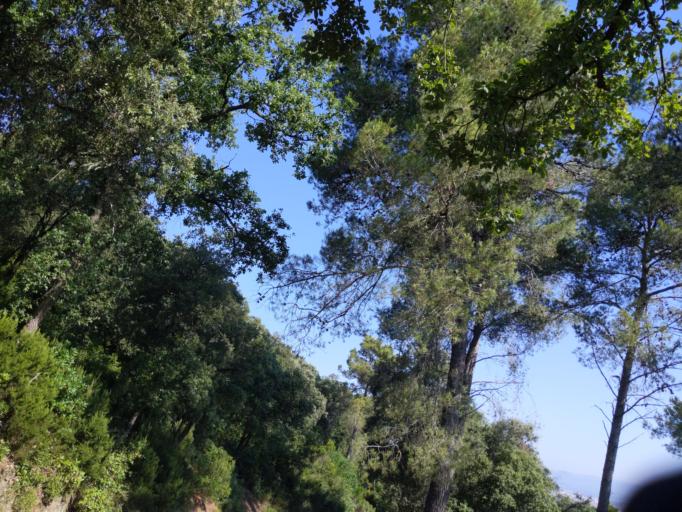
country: ES
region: Catalonia
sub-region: Provincia de Barcelona
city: Cerdanyola del Valles
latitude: 41.4629
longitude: 2.1363
